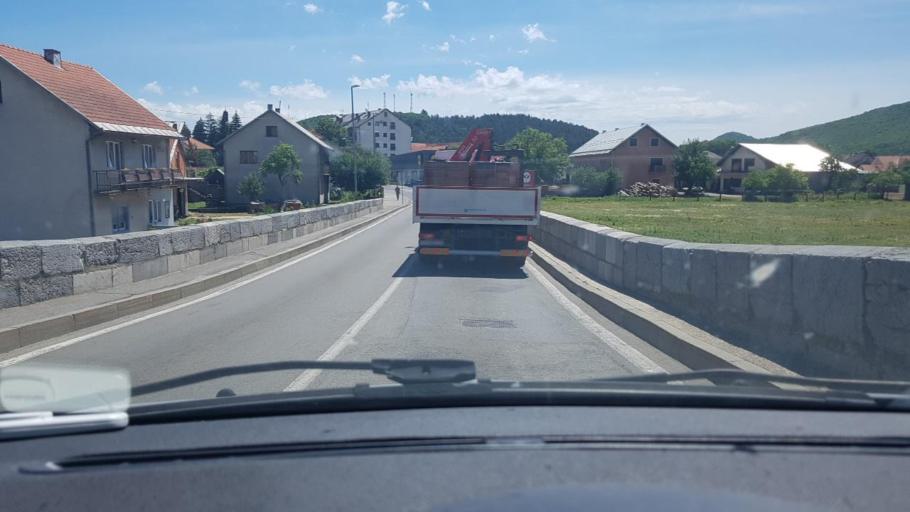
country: HR
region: Licko-Senjska
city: Otocac
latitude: 44.8695
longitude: 15.2306
